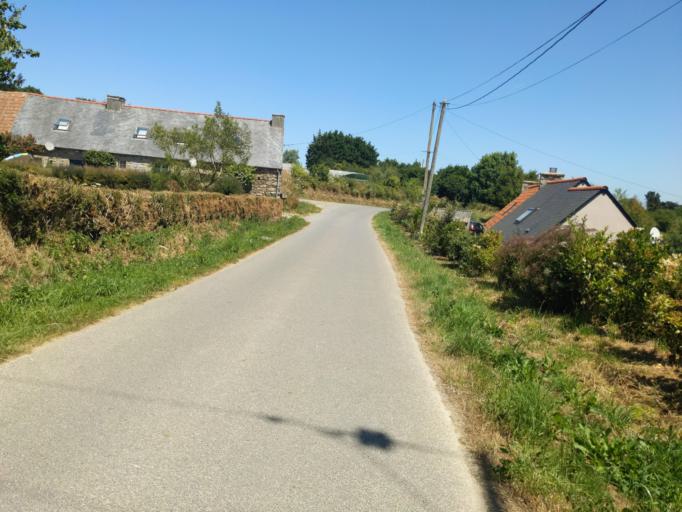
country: FR
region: Brittany
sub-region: Departement des Cotes-d'Armor
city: Plouguiel
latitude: 48.8097
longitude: -3.2174
